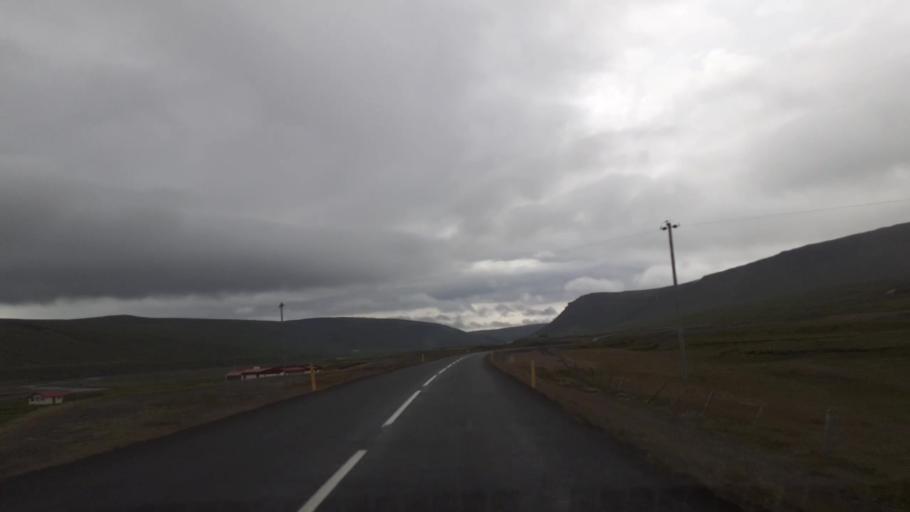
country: IS
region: East
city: Egilsstadir
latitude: 65.6305
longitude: -15.0610
